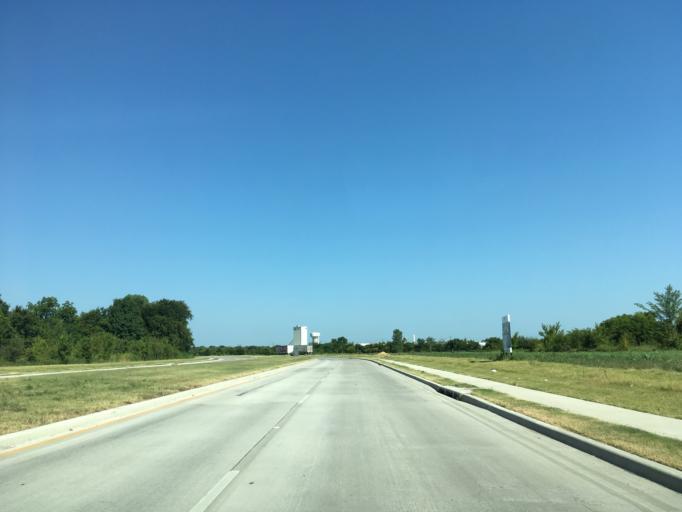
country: US
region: Texas
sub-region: Collin County
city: Fairview
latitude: 33.1691
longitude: -96.6041
